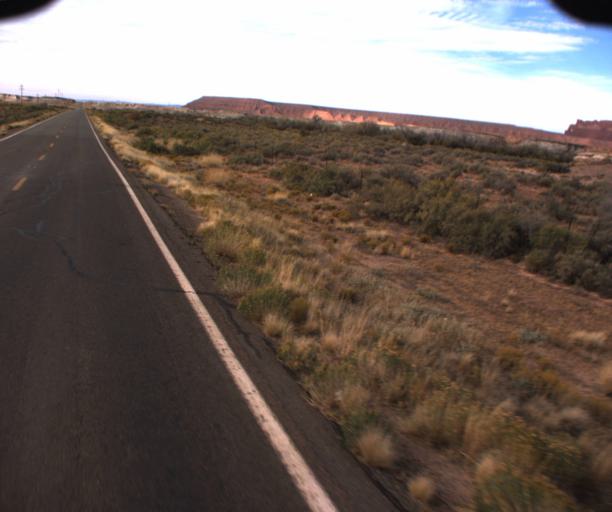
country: US
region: Arizona
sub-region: Apache County
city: Many Farms
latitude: 36.4969
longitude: -109.4883
